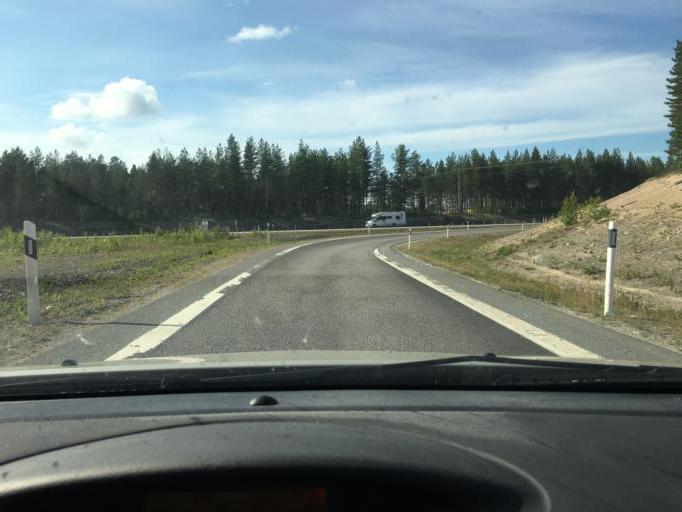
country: SE
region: Norrbotten
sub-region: Lulea Kommun
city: Gammelstad
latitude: 65.5984
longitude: 22.0474
